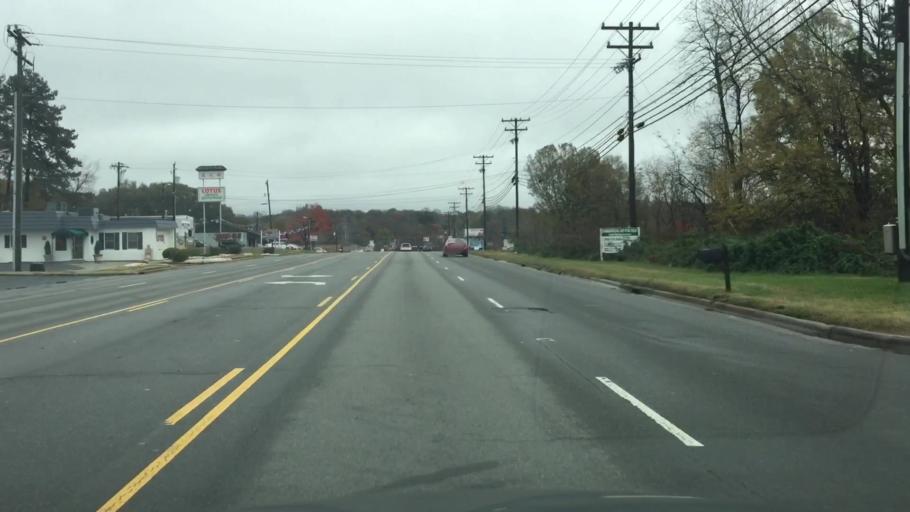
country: US
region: North Carolina
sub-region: Iredell County
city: Mooresville
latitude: 35.5887
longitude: -80.8343
